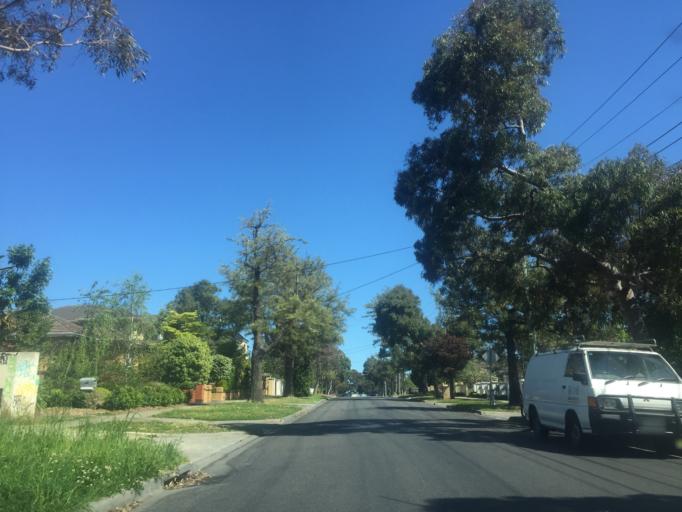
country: AU
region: Victoria
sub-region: Boroondara
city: Canterbury
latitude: -37.8073
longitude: 145.0852
